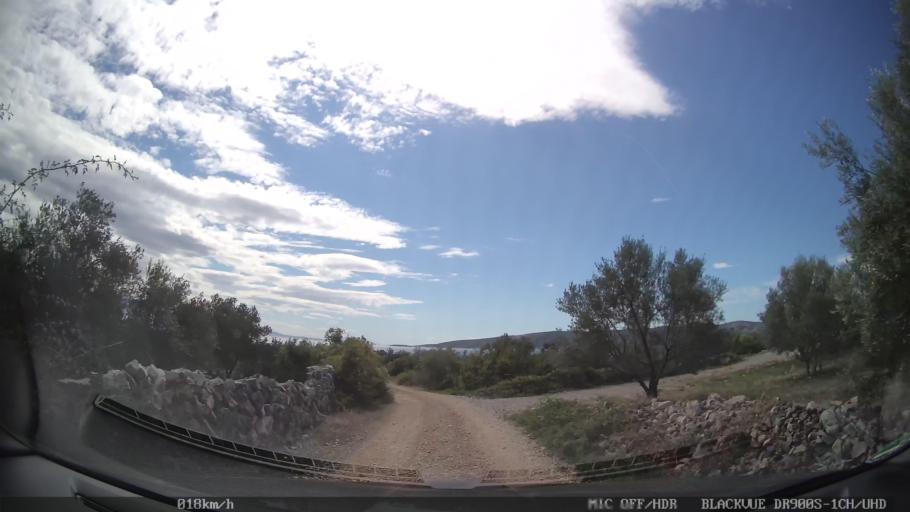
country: HR
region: Primorsko-Goranska
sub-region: Grad Krk
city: Krk
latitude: 45.0187
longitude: 14.5244
